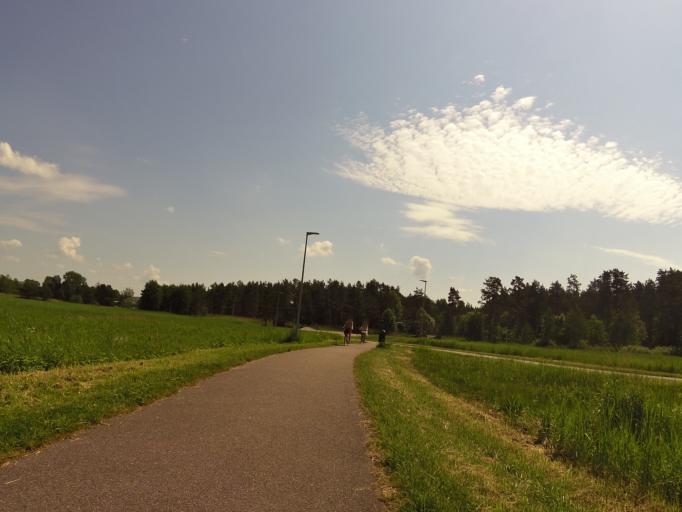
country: EE
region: Laeaene
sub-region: Haapsalu linn
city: Haapsalu
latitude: 58.9396
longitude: 23.5213
